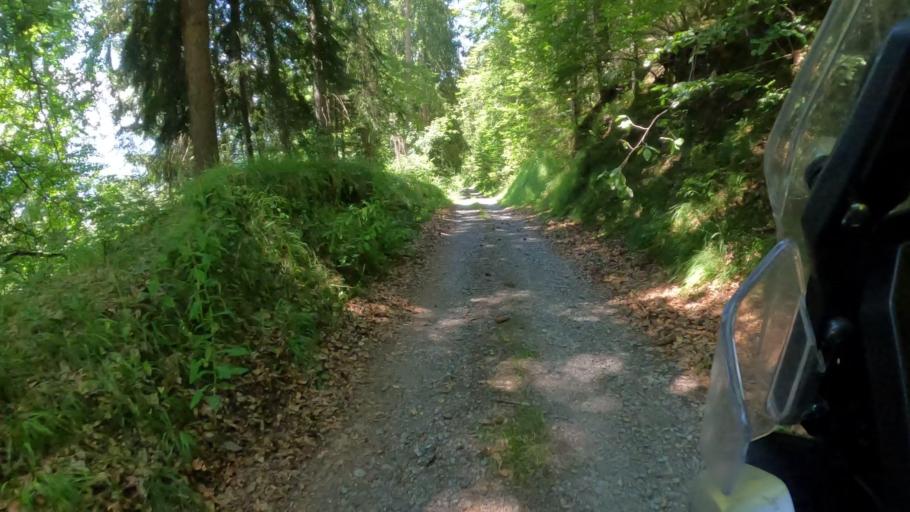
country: CH
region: Vaud
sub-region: Aigle District
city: Villars-sur-Ollon
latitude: 46.2911
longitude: 7.0678
